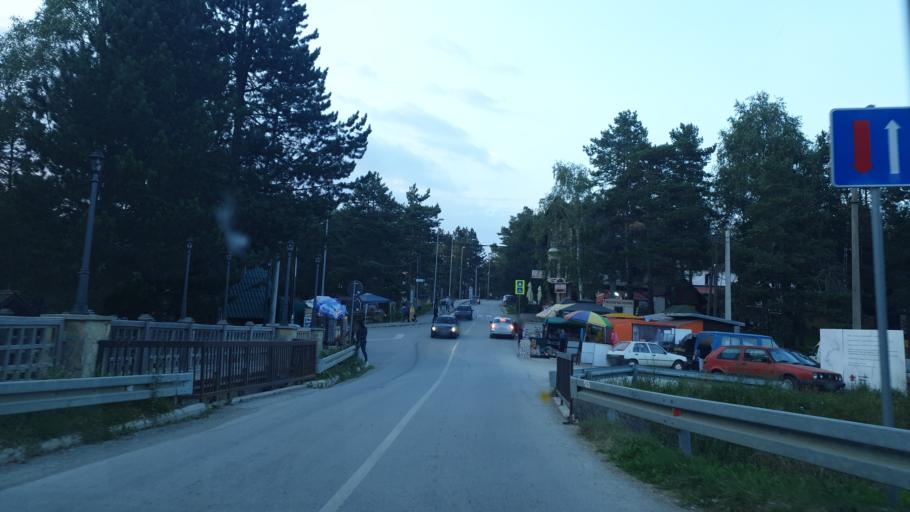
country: RS
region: Central Serbia
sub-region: Zlatiborski Okrug
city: Kosjeric
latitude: 44.1041
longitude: 19.9917
